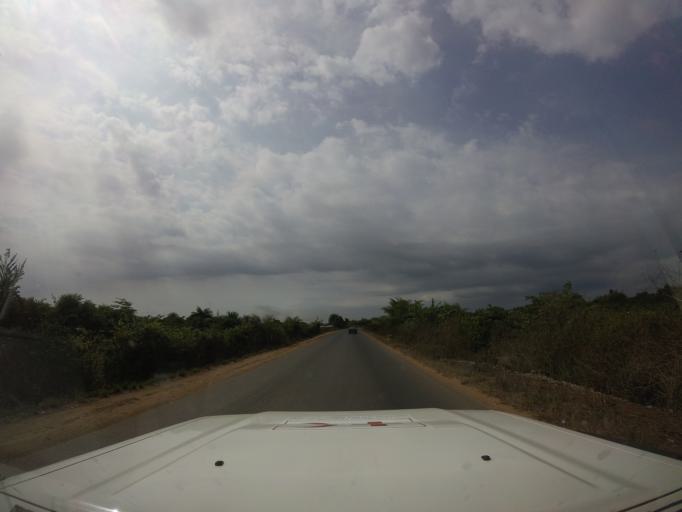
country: LR
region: Montserrado
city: Monrovia
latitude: 6.4634
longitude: -10.8071
